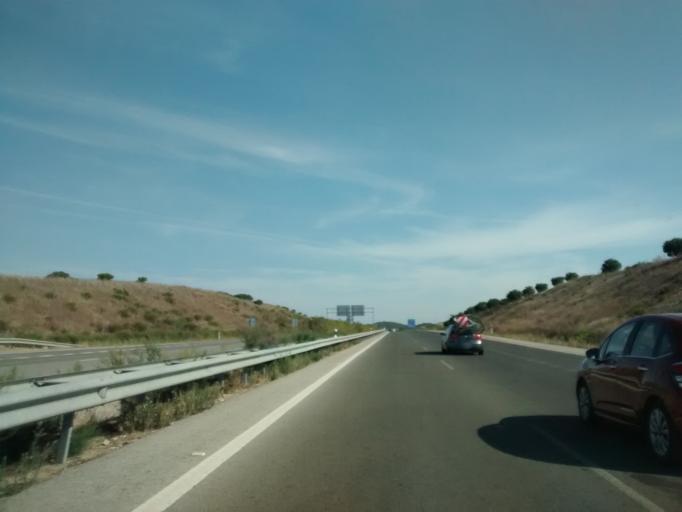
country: ES
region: Andalusia
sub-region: Provincia de Cadiz
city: Conil de la Frontera
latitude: 36.2974
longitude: -6.0569
